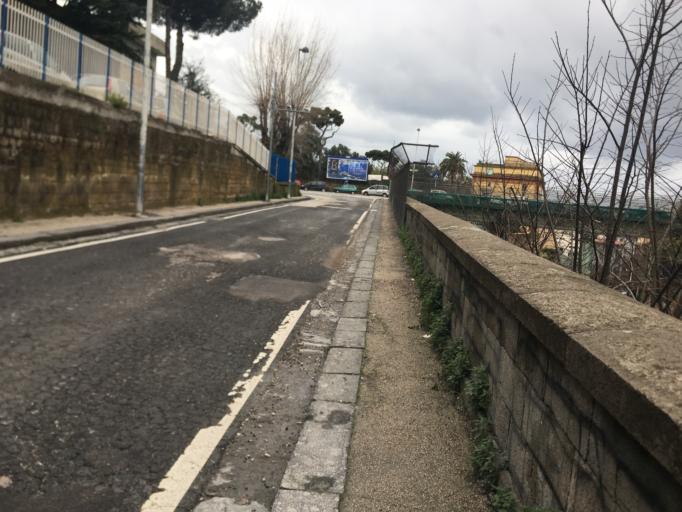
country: IT
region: Campania
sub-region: Provincia di Napoli
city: Napoli
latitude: 40.8592
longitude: 14.2258
